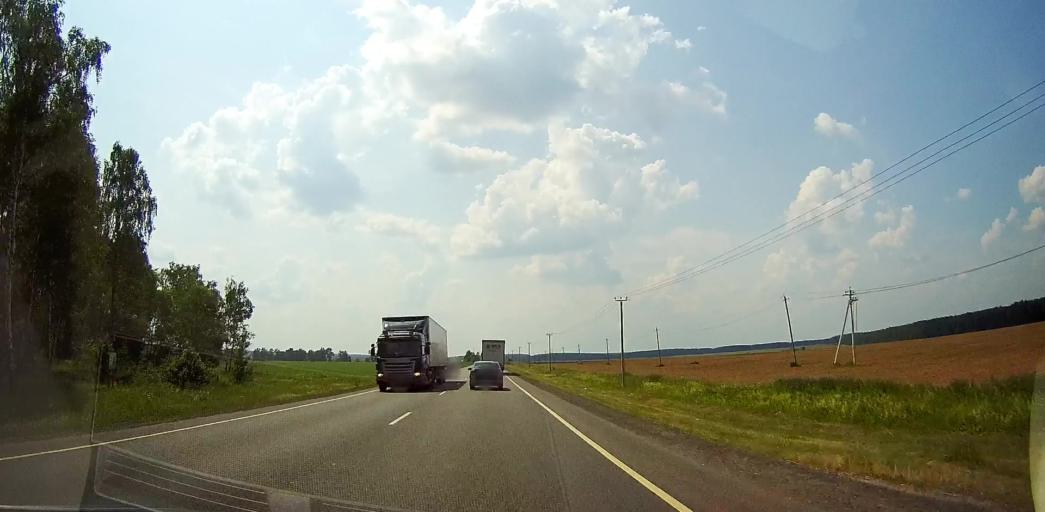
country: RU
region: Moskovskaya
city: Malino
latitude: 55.1356
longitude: 38.2642
